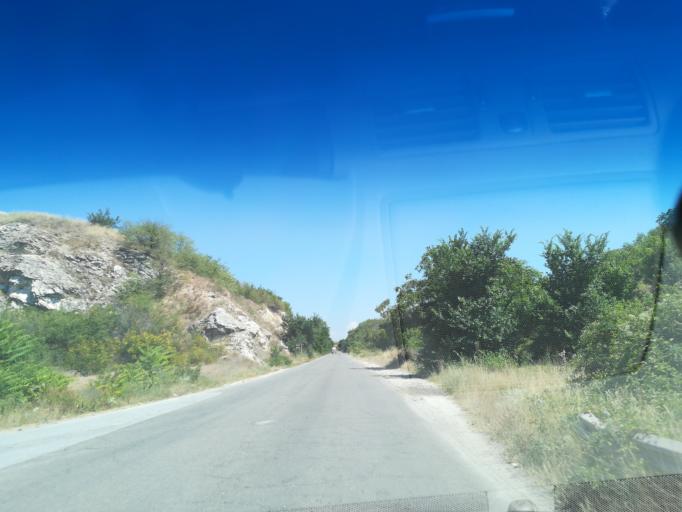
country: BG
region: Plovdiv
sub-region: Obshtina Sadovo
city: Sadovo
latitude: 42.0257
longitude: 24.9888
